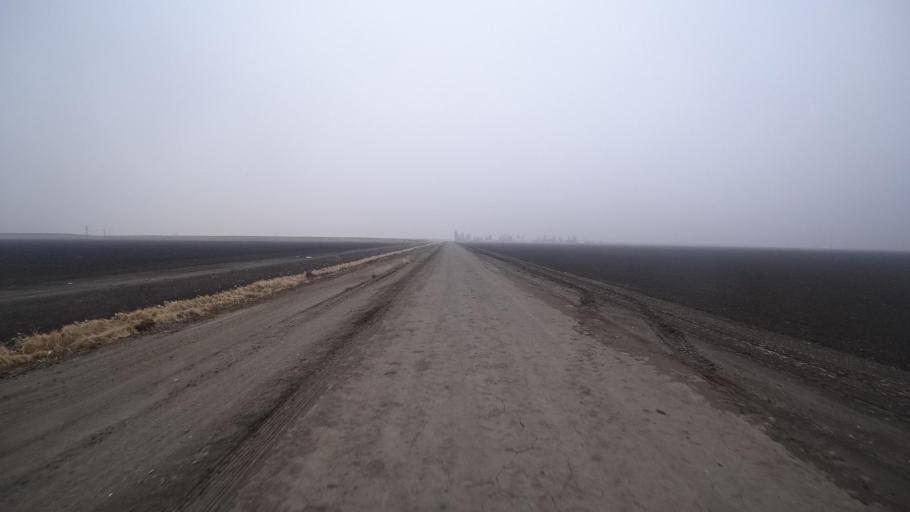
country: US
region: California
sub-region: Kern County
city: Buttonwillow
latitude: 35.4123
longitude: -119.5104
